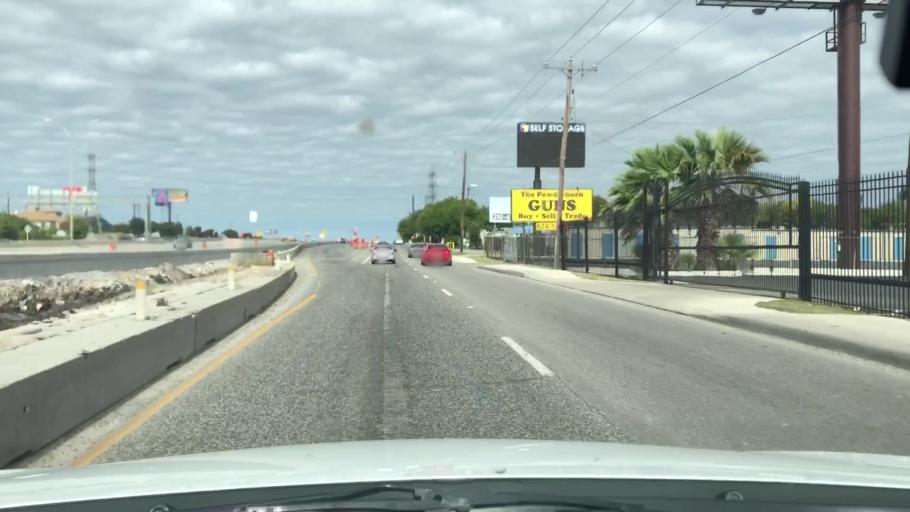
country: US
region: Texas
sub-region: Bexar County
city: Lackland Air Force Base
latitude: 29.4074
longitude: -98.6493
